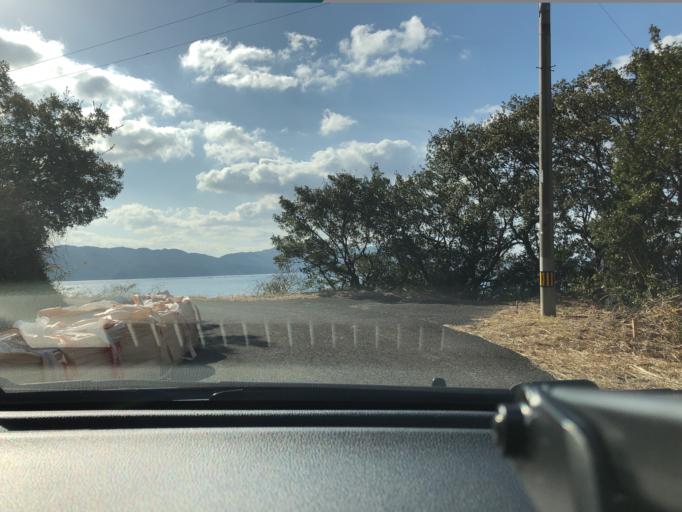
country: JP
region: Kochi
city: Sukumo
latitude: 32.9132
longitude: 132.6894
